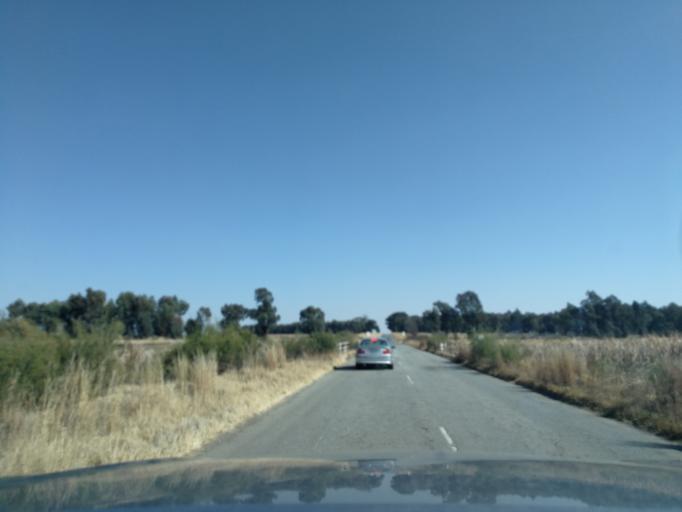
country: ZA
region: North-West
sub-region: Dr Kenneth Kaunda District Municipality
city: Orkney
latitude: -27.0513
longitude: 26.7283
